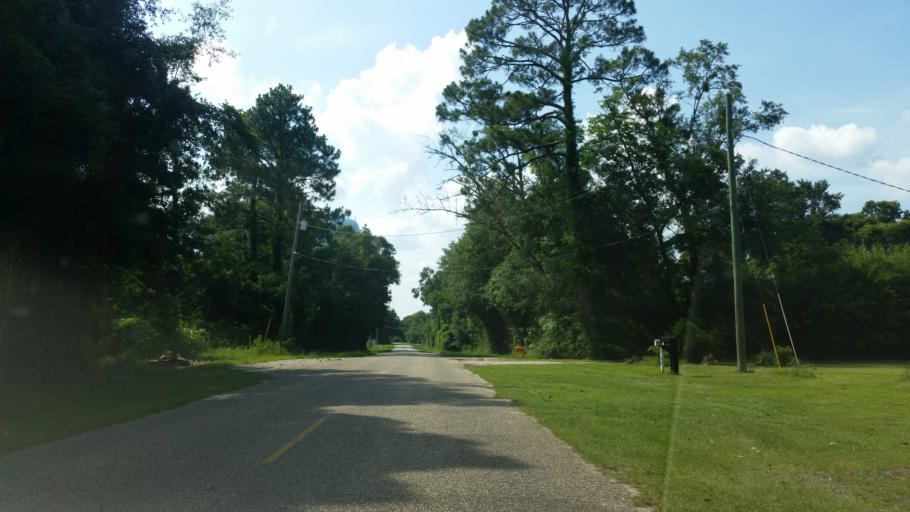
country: US
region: Florida
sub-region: Escambia County
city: Gonzalez
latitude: 30.5821
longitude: -87.2952
